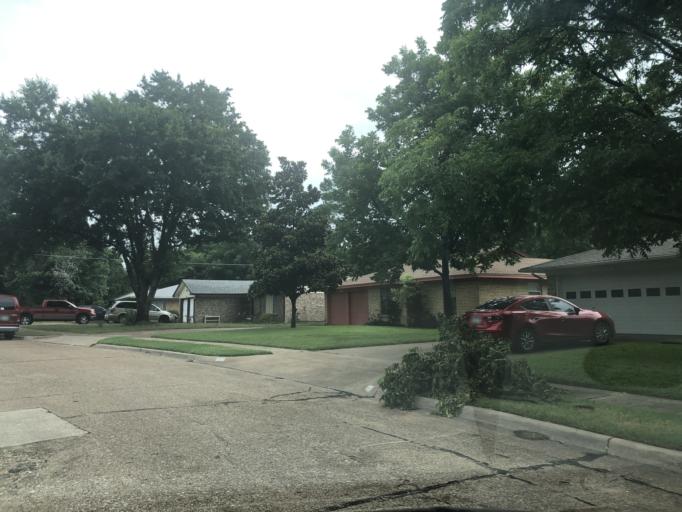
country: US
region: Texas
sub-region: Dallas County
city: Irving
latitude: 32.8040
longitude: -96.9436
